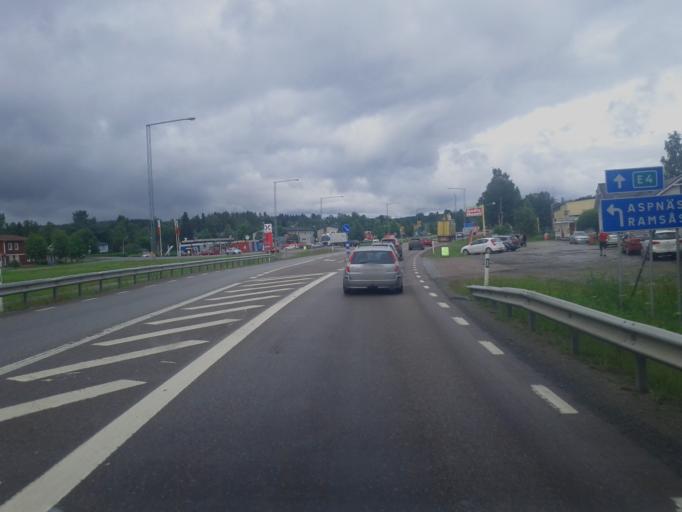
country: SE
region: Vaesternorrland
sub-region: Haernoesands Kommun
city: Haernoesand
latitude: 62.6725
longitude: 17.8399
